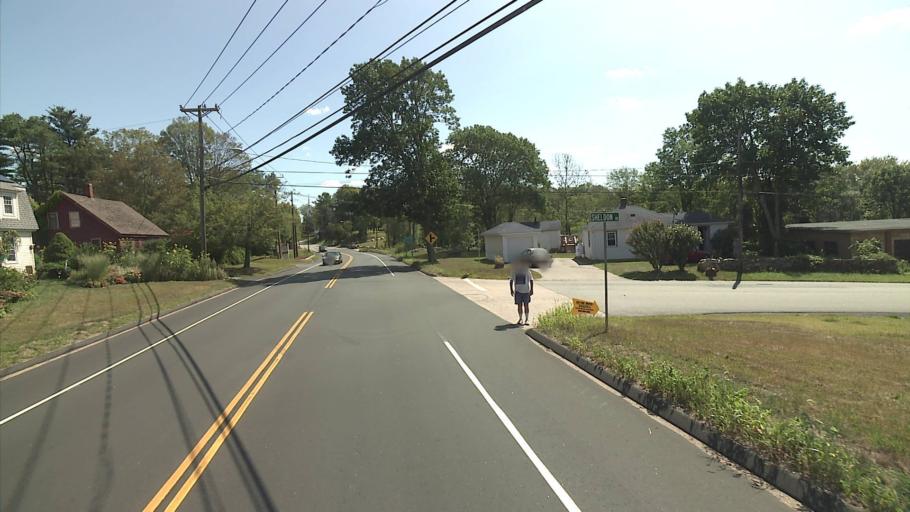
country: US
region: Connecticut
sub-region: New London County
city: Preston City
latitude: 41.5728
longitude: -71.8747
